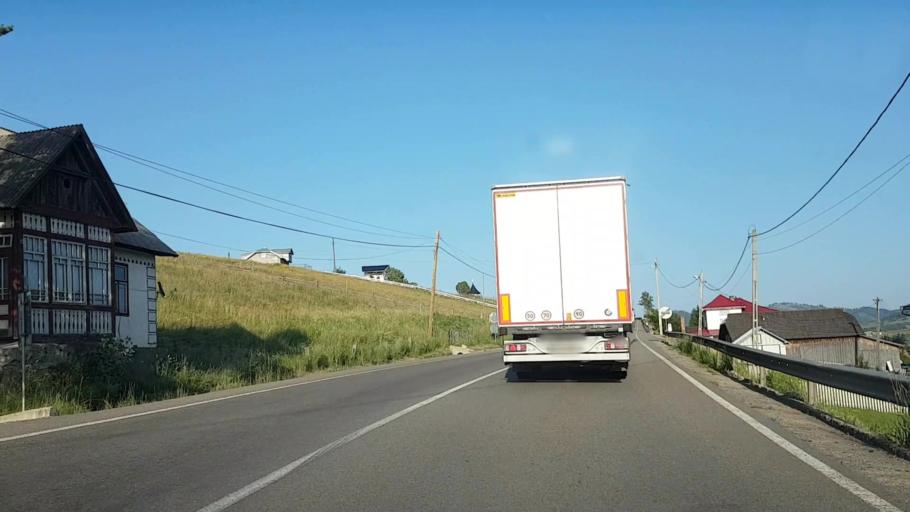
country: RO
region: Suceava
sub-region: Comuna Cosna
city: Cosna
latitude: 47.3623
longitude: 25.2068
